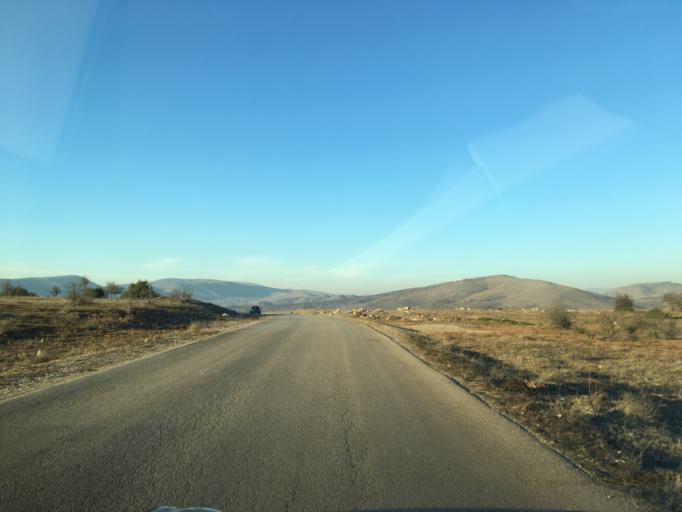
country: GR
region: West Macedonia
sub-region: Nomos Kozanis
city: Kozani
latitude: 40.2751
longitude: 21.7348
